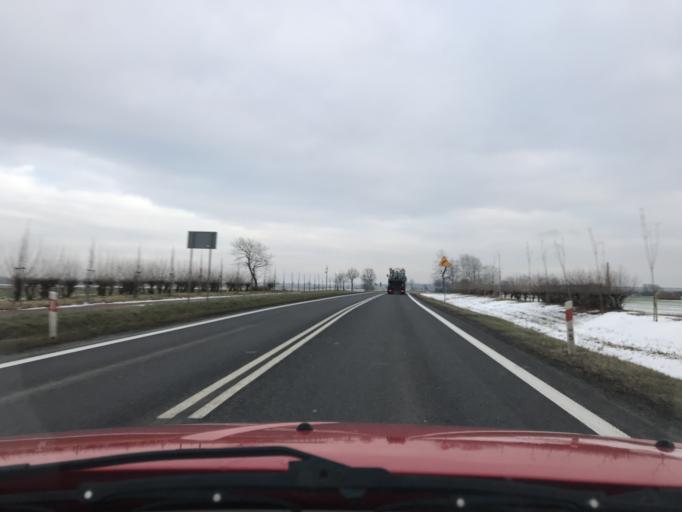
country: PL
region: Greater Poland Voivodeship
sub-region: Powiat pleszewski
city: Goluchow
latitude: 51.8808
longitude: 17.8726
